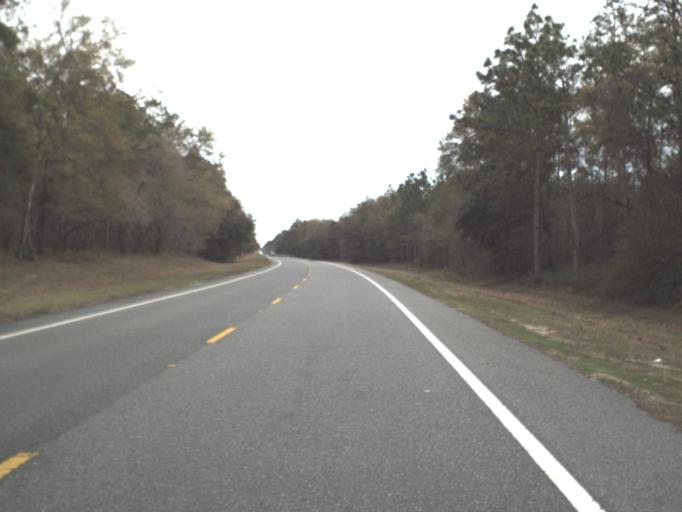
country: US
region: Florida
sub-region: Wakulla County
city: Crawfordville
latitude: 30.2911
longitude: -84.4067
